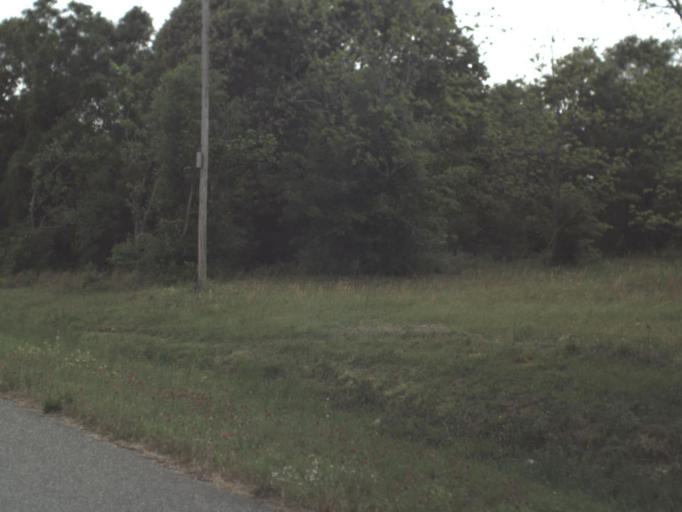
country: US
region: Alabama
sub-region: Escambia County
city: East Brewton
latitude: 30.8959
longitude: -87.0425
